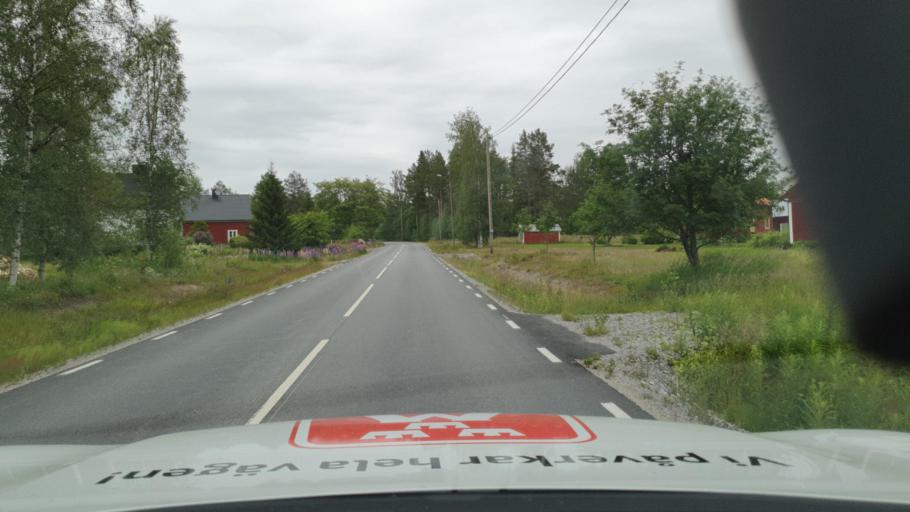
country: SE
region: Vaesterbotten
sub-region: Nordmalings Kommun
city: Nordmaling
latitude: 63.5011
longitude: 19.3268
